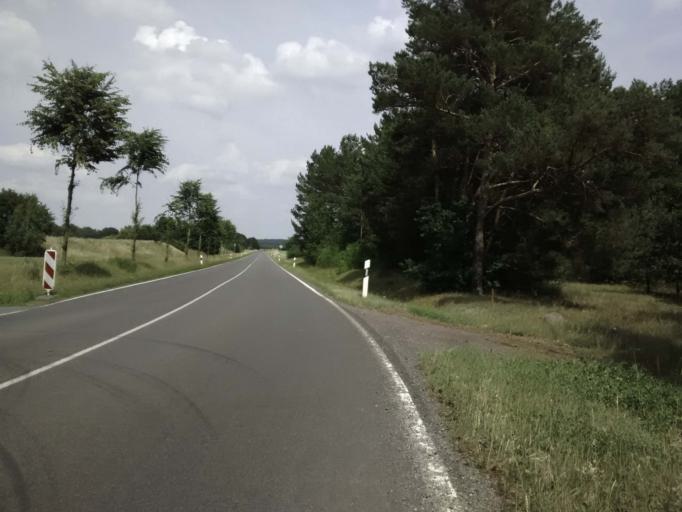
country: DE
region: Saxony-Anhalt
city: Hohenwarthe
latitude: 52.2495
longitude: 11.7442
